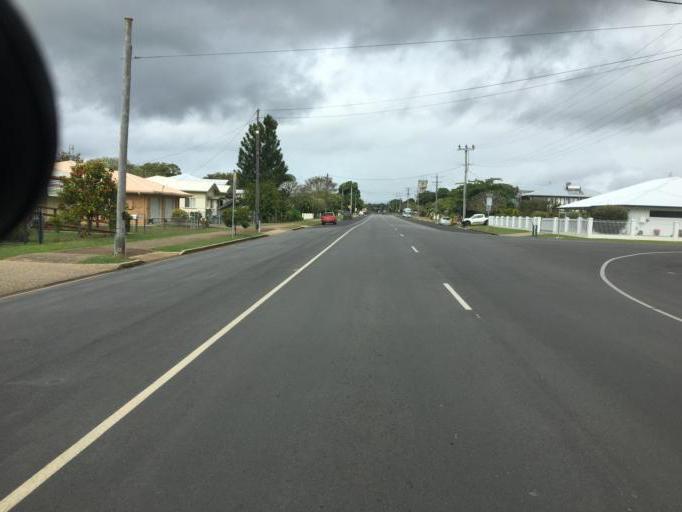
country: AU
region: Queensland
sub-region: Tablelands
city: Mareeba
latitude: -16.9967
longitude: 145.4255
